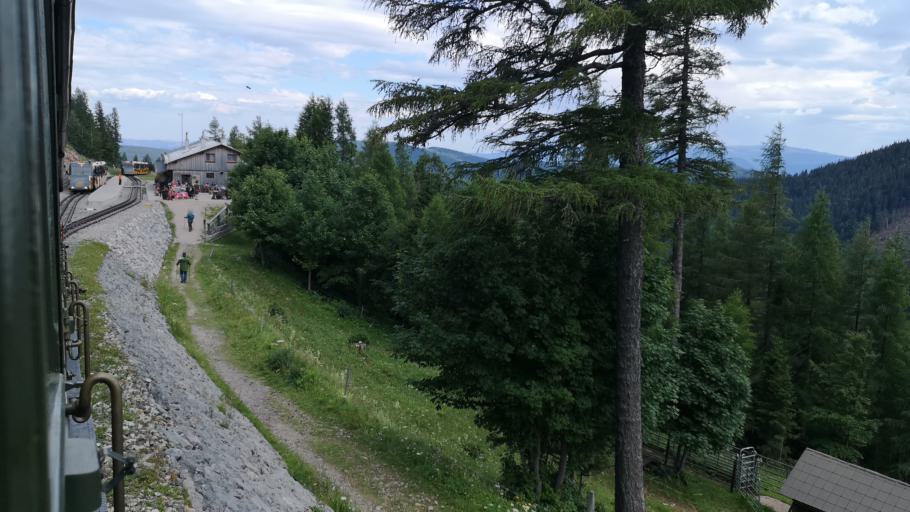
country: AT
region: Lower Austria
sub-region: Politischer Bezirk Neunkirchen
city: Reichenau an der Rax
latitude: 47.7538
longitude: 15.8497
